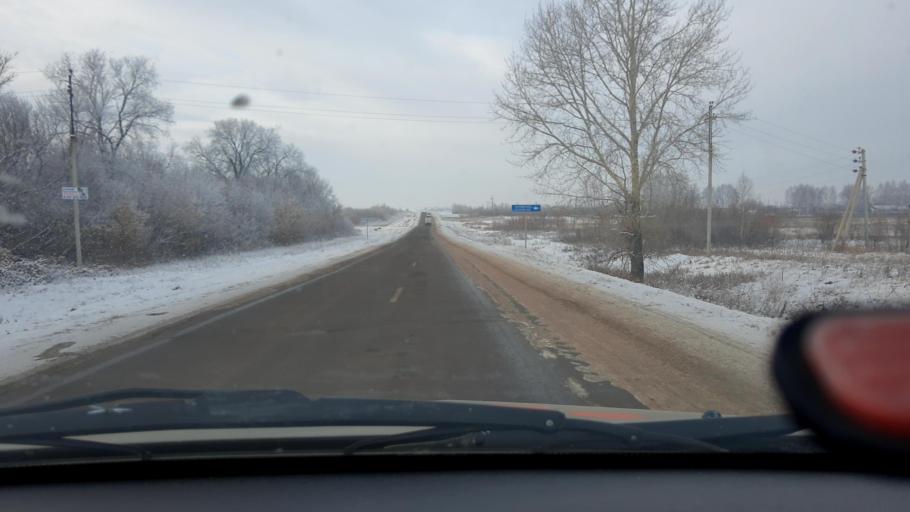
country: RU
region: Bashkortostan
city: Avdon
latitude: 54.3638
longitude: 55.8321
